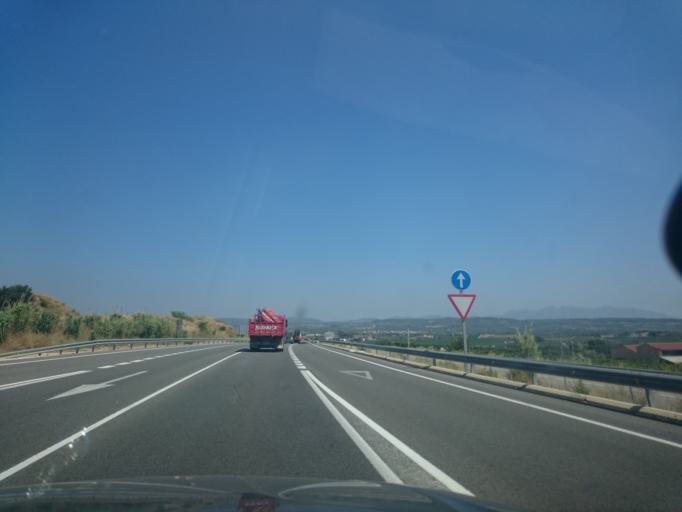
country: ES
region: Catalonia
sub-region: Provincia de Barcelona
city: La Granada
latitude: 41.3852
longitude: 1.7096
